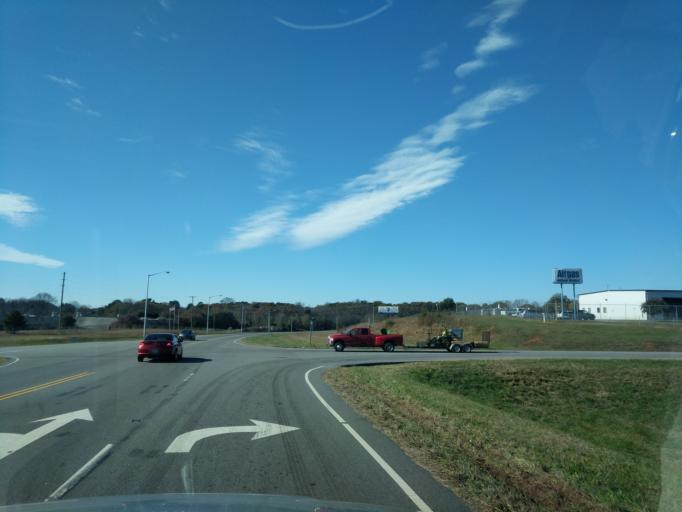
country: US
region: North Carolina
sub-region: Iredell County
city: Statesville
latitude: 35.7848
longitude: -80.9231
